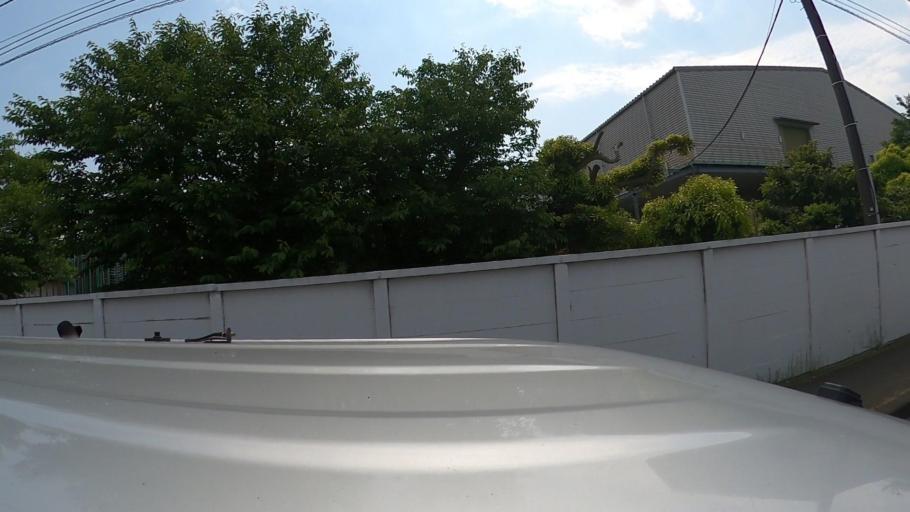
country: JP
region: Kanagawa
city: Chigasaki
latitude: 35.3620
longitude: 139.3733
